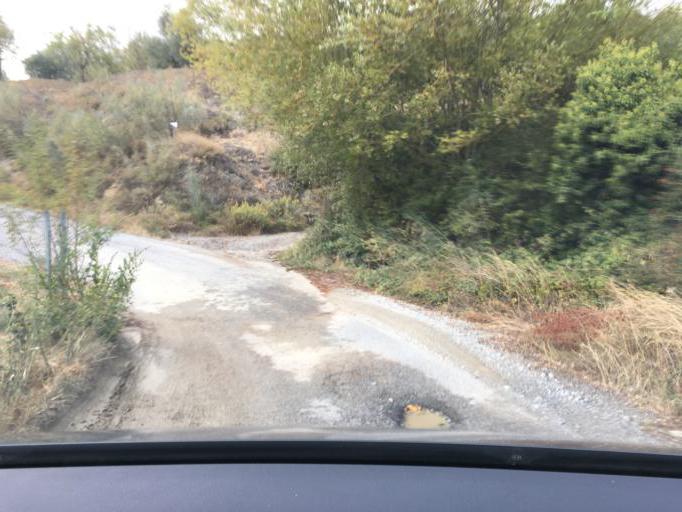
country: ES
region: Andalusia
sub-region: Provincia de Granada
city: Quentar
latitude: 37.1980
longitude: -3.4647
